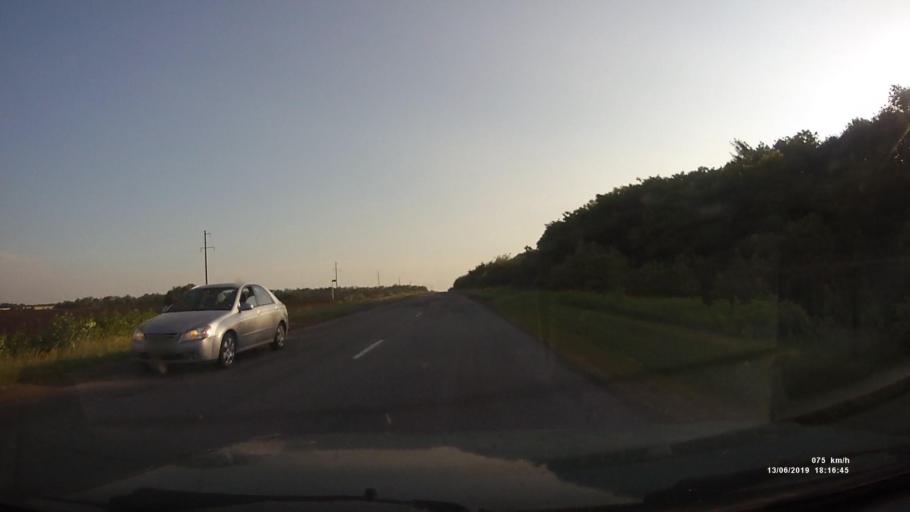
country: RU
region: Rostov
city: Kazanskaya
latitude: 49.9257
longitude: 41.3343
